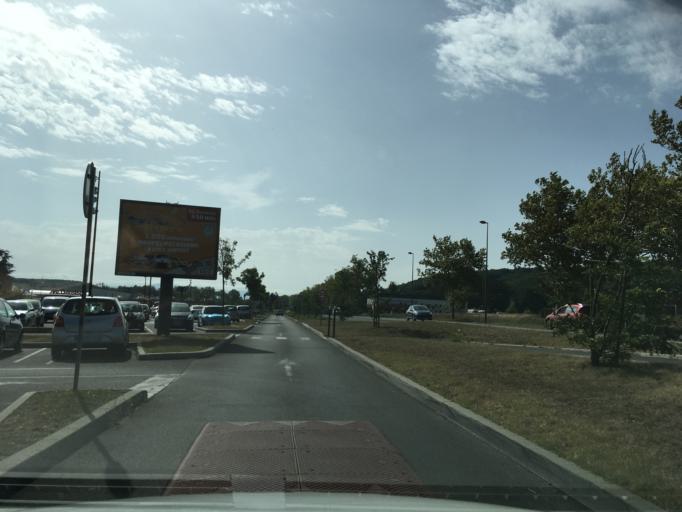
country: FR
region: Midi-Pyrenees
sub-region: Departement du Tarn
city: Lagarrigue
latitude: 43.5920
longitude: 2.2673
